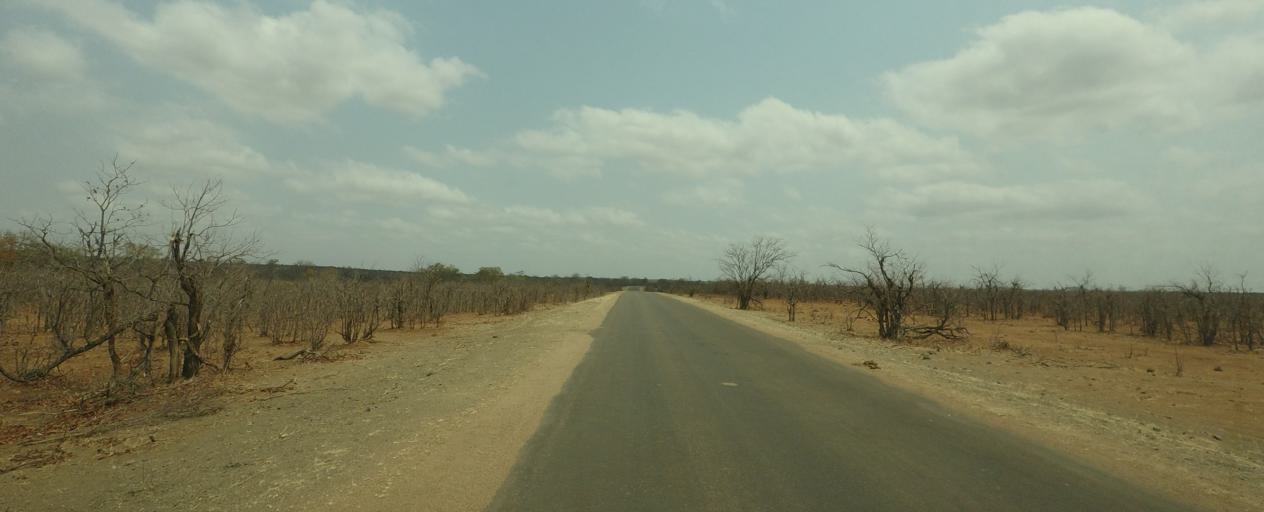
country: ZA
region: Limpopo
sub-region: Mopani District Municipality
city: Phalaborwa
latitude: -23.5525
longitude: 31.4375
